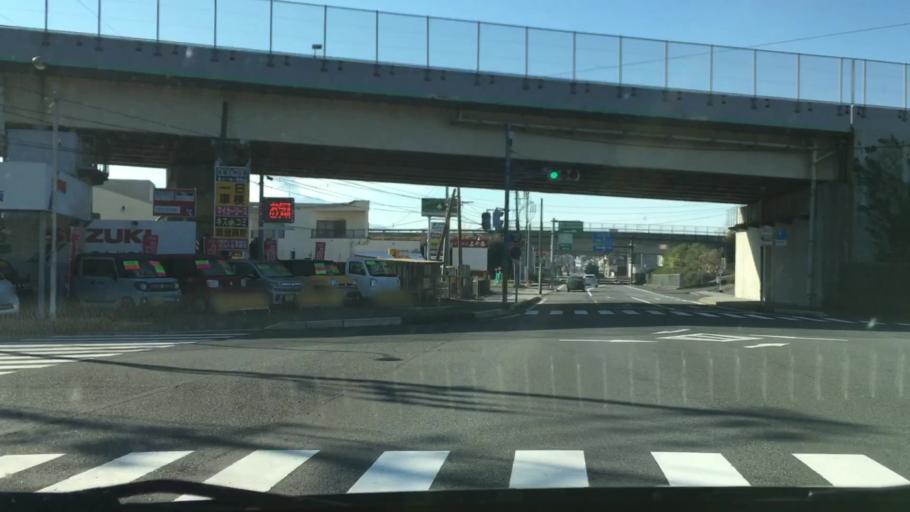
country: JP
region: Kagoshima
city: Kajiki
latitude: 31.7475
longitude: 130.6708
